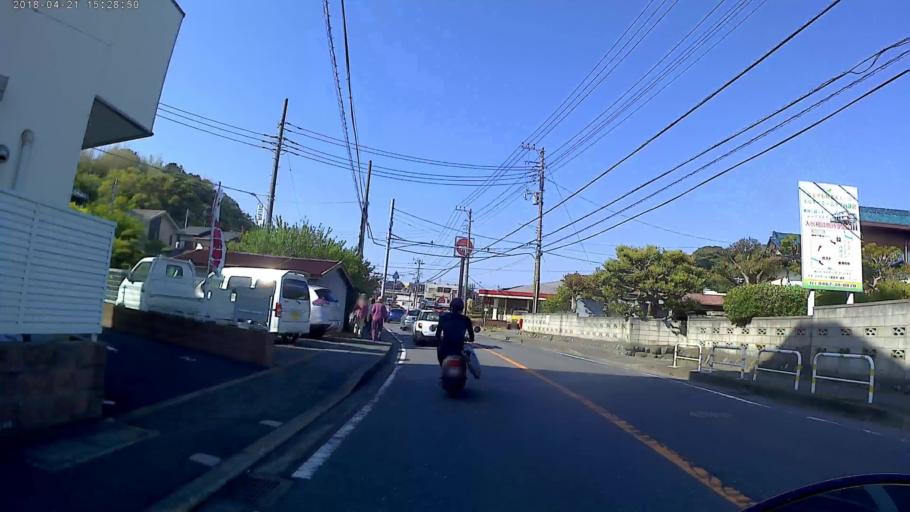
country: JP
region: Kanagawa
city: Fujisawa
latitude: 35.3161
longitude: 139.5029
